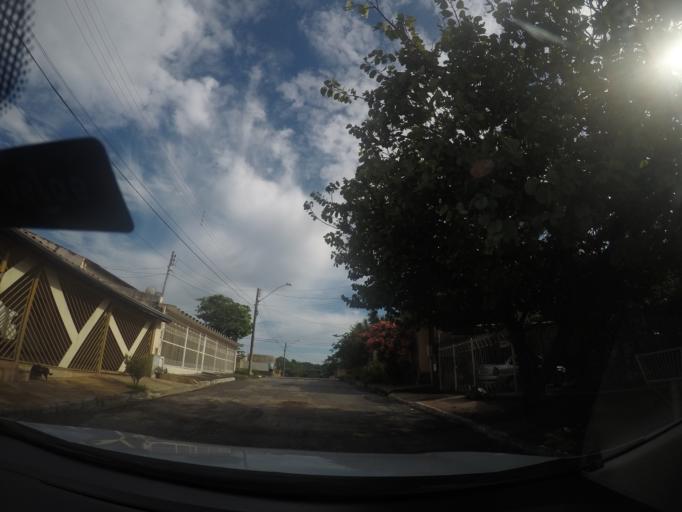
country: BR
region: Goias
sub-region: Goiania
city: Goiania
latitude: -16.6934
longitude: -49.2010
